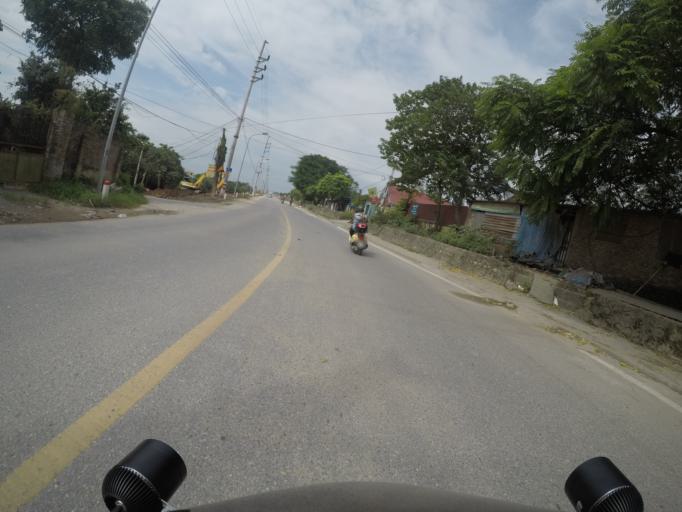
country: VN
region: Ha Noi
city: Tay Ho
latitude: 21.0915
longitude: 105.7694
